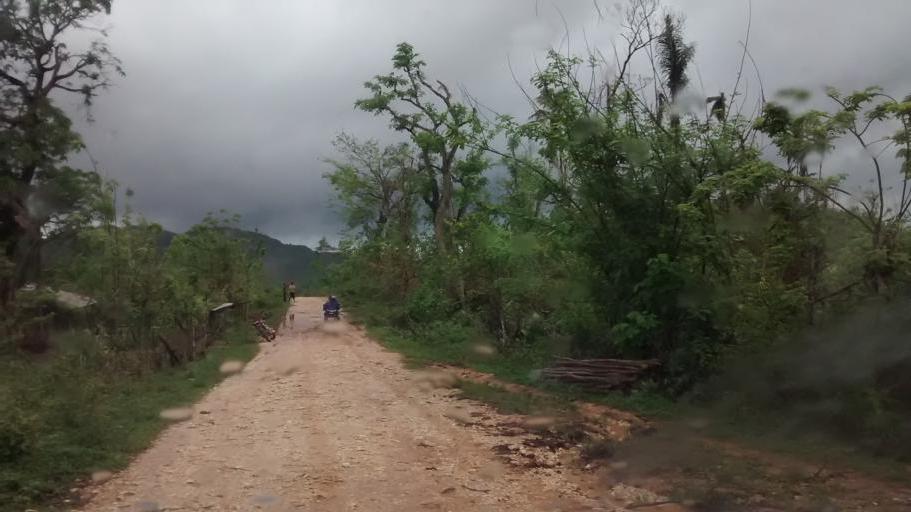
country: HT
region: Grandans
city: Corail
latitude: 18.5366
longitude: -73.9898
